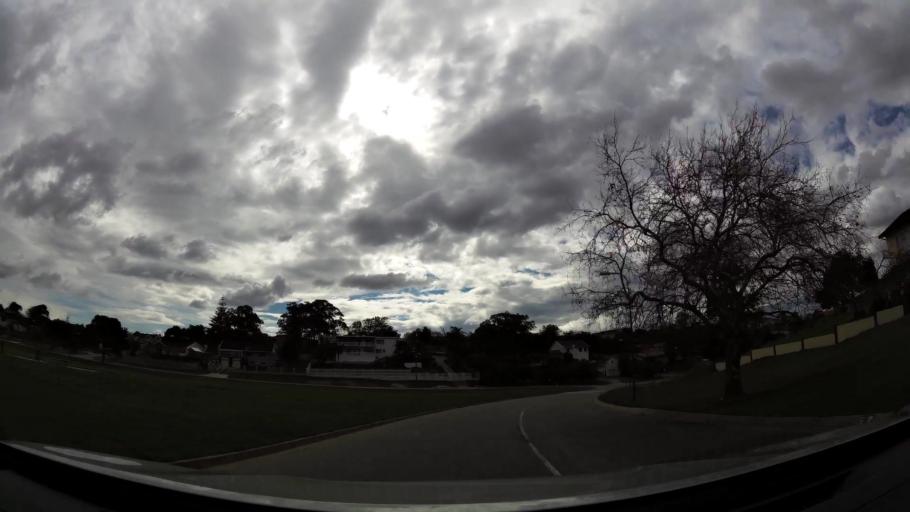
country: ZA
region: Eastern Cape
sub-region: Nelson Mandela Bay Metropolitan Municipality
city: Port Elizabeth
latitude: -33.9372
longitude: 25.5181
